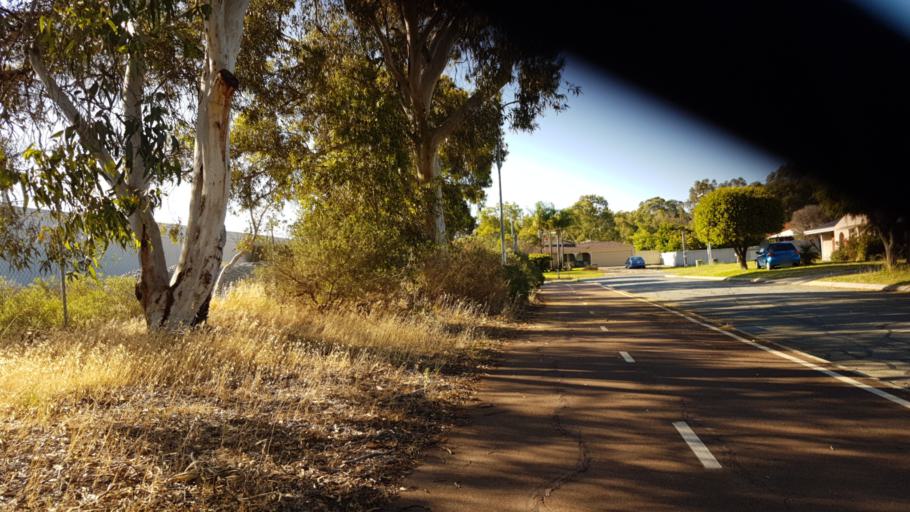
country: AU
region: Western Australia
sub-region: Gosnells
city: Kenwick
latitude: -32.0394
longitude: 115.9730
